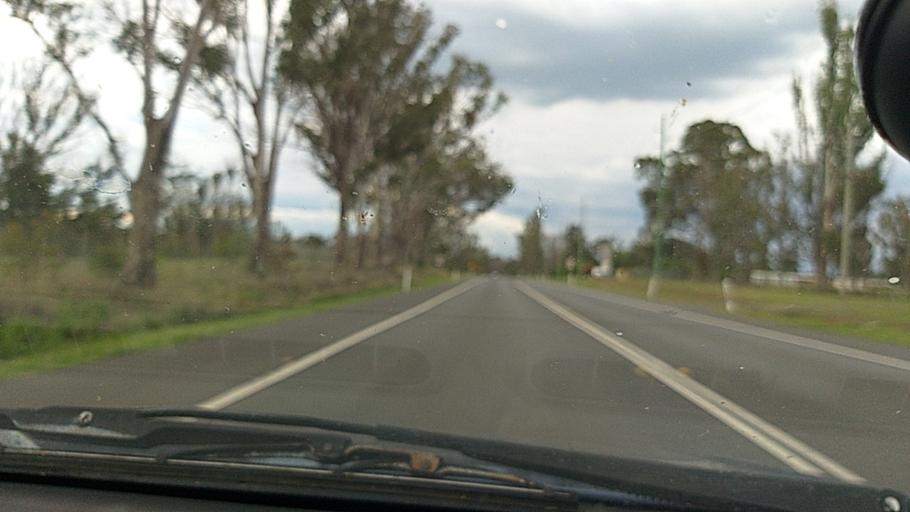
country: AU
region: New South Wales
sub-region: Penrith Municipality
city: Glenmore Park
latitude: -33.8222
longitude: 150.6849
